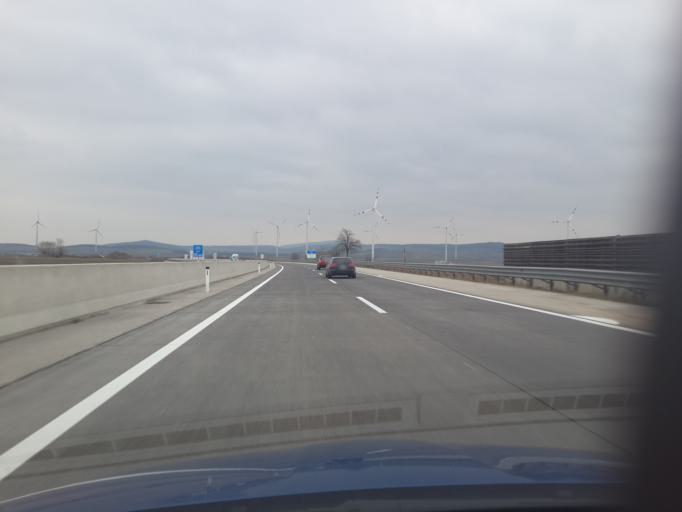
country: AT
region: Burgenland
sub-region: Politischer Bezirk Neusiedl am See
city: Kittsee
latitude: 48.0798
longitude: 17.0479
